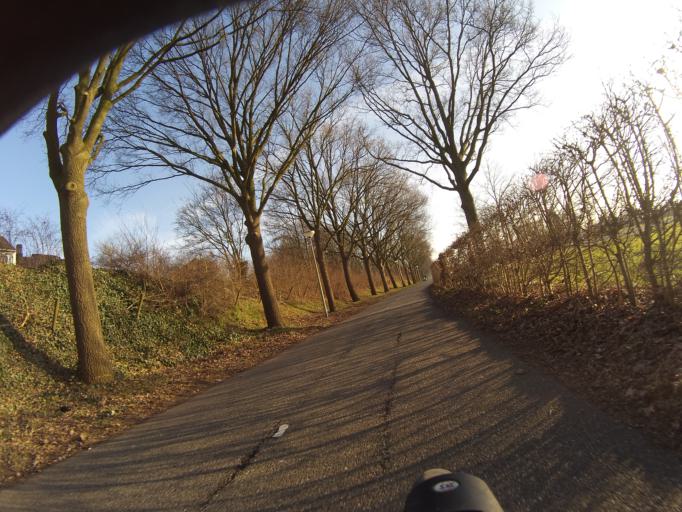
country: NL
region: Utrecht
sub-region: Gemeente Amersfoort
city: Hoogland
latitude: 52.1864
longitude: 5.3690
